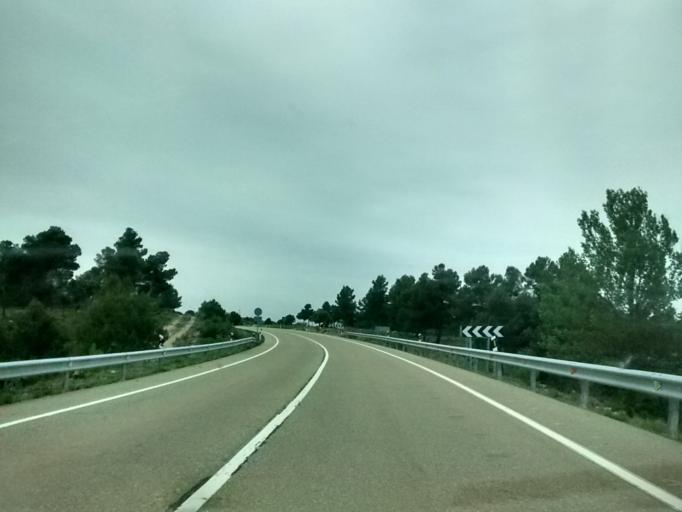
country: ES
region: Aragon
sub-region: Provincia de Teruel
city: Fornoles
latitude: 40.8979
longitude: -0.0322
